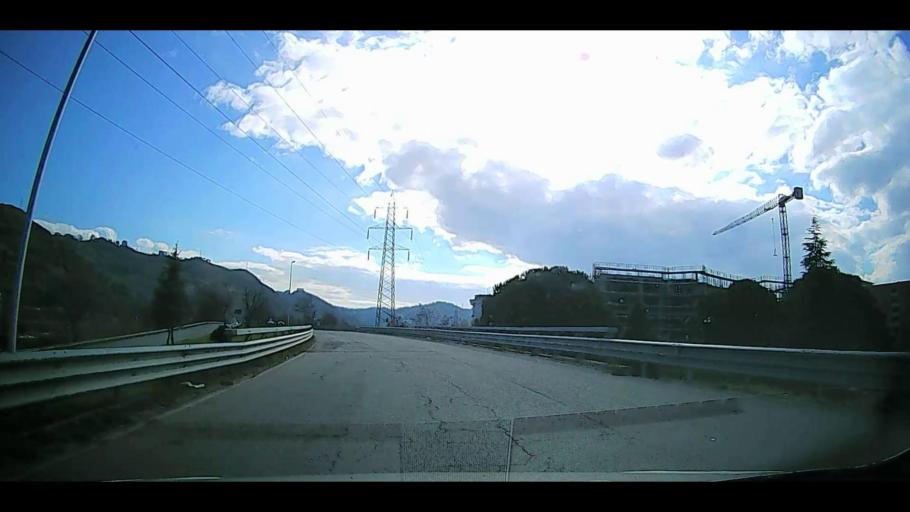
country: IT
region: Calabria
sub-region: Provincia di Cosenza
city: Cosenza
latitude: 39.3142
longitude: 16.2586
